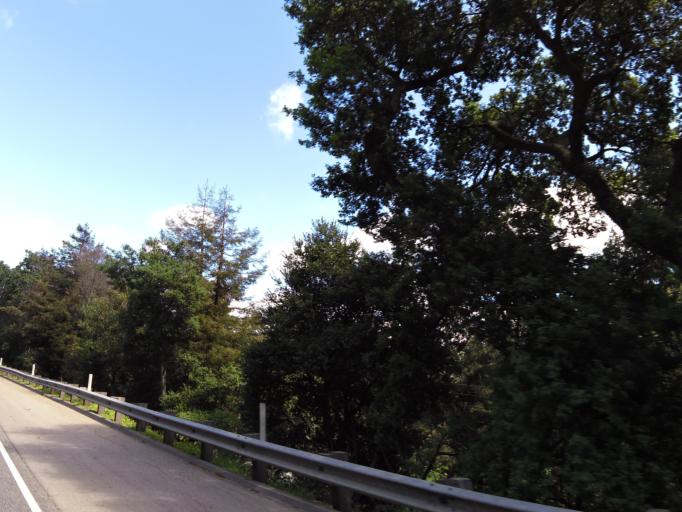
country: US
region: California
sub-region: Santa Cruz County
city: Pasatiempo
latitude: 37.0062
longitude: -122.0208
